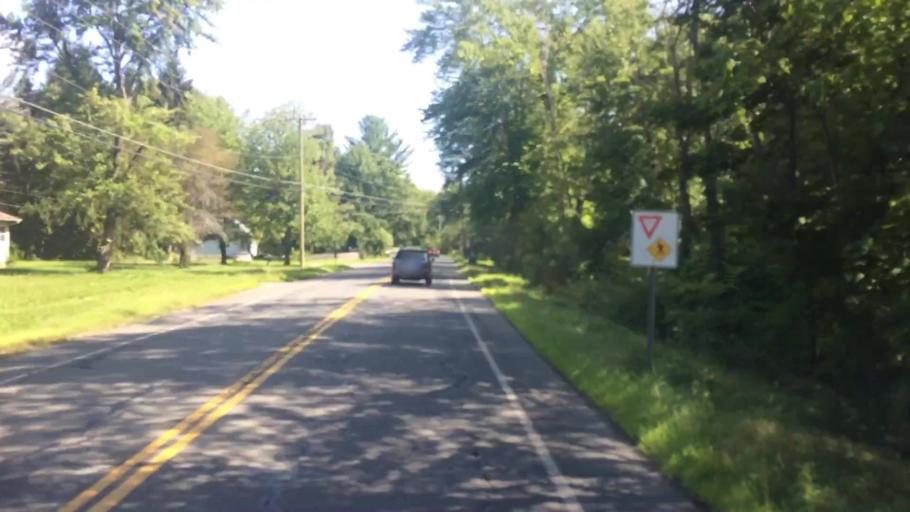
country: US
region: Massachusetts
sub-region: Hampshire County
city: South Amherst
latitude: 42.3534
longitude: -72.5226
